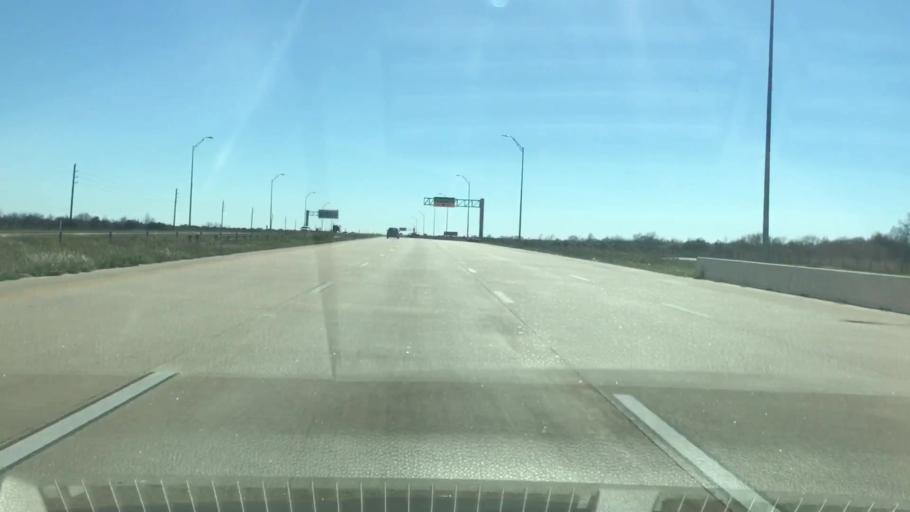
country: US
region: Texas
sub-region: Harris County
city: Cypress
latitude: 29.9882
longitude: -95.7695
